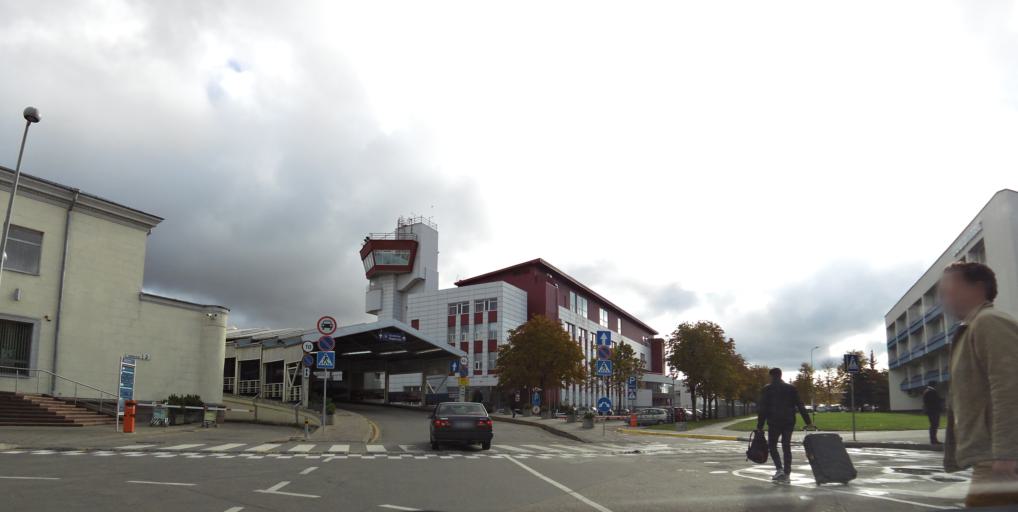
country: LT
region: Vilnius County
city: Naujamiestis
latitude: 54.6426
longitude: 25.2793
